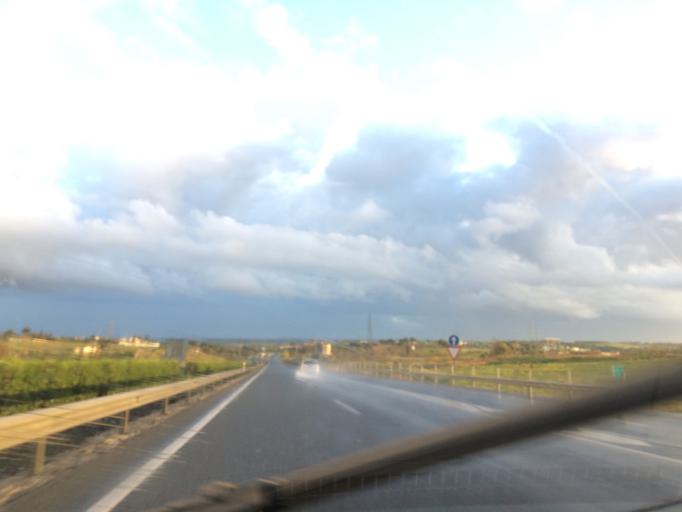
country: ES
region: Andalusia
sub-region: Provincia de Sevilla
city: Alcala de Guadaira
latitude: 37.3407
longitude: -5.8211
